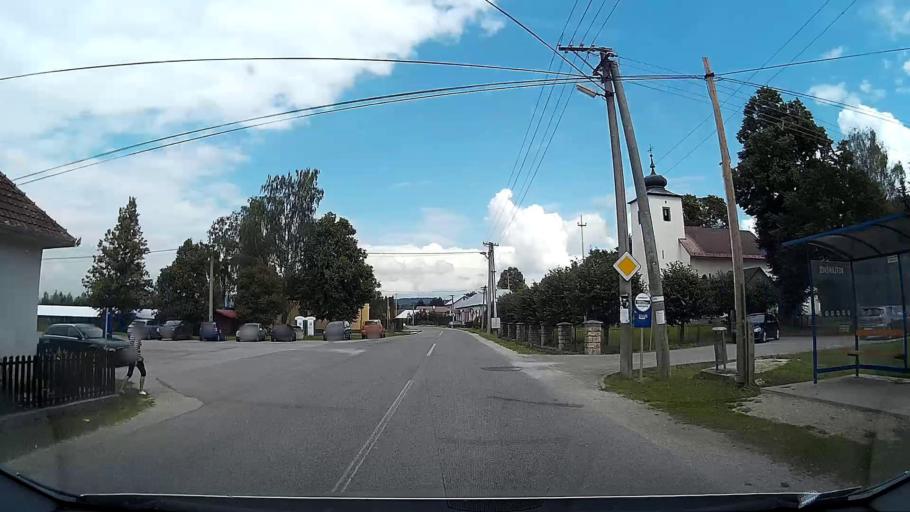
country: SK
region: Presovsky
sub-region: Okres Poprad
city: Poprad
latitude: 48.9797
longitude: 20.3907
